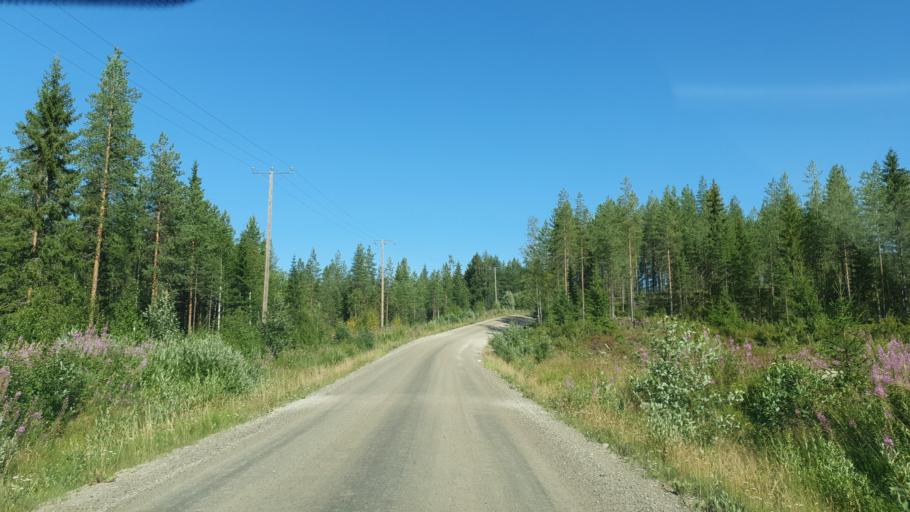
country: FI
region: Kainuu
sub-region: Kehys-Kainuu
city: Kuhmo
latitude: 64.0497
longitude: 29.6112
